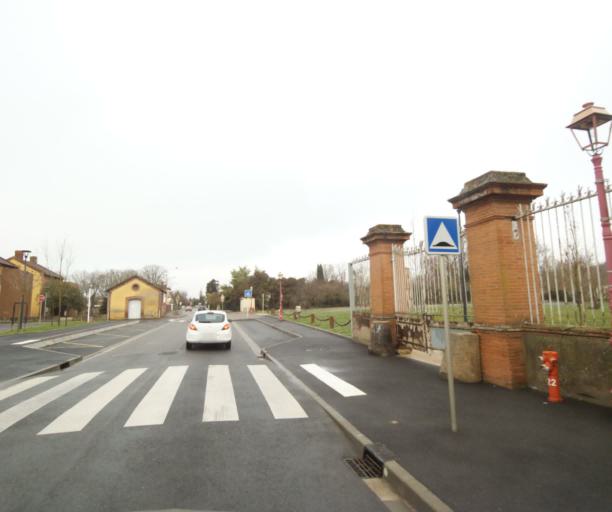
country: FR
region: Midi-Pyrenees
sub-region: Departement de la Haute-Garonne
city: Villemur-sur-Tarn
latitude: 43.8628
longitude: 1.5018
